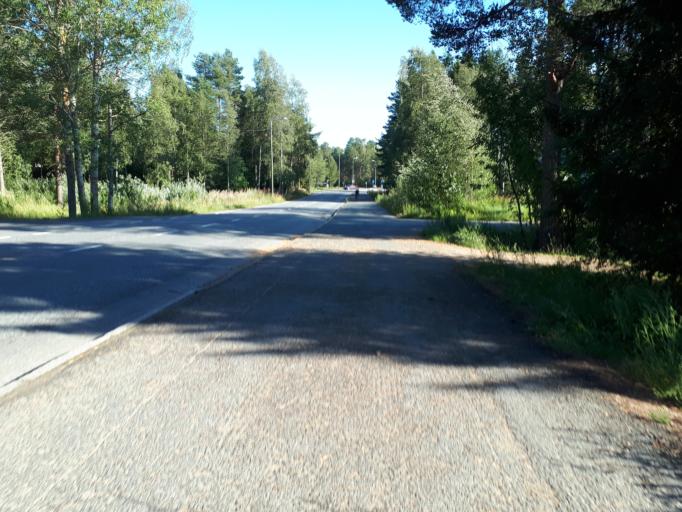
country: FI
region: Northern Ostrobothnia
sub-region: Oulunkaari
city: Ii
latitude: 65.3178
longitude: 25.3855
